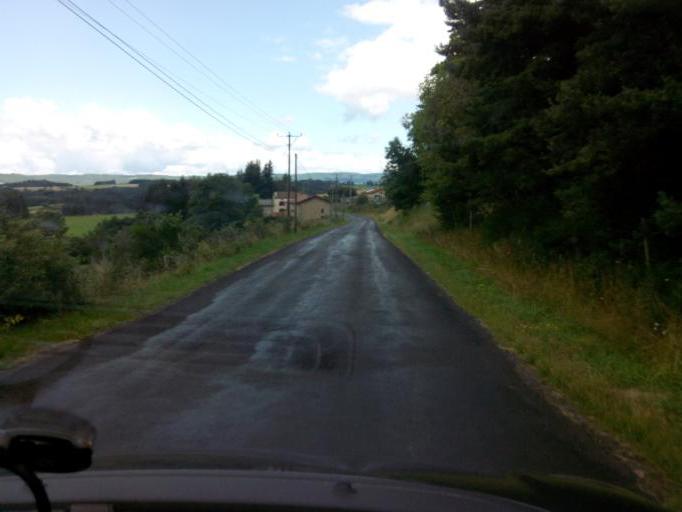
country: FR
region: Rhone-Alpes
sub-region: Departement de la Loire
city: Usson-en-Forez
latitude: 45.3762
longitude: 3.9499
